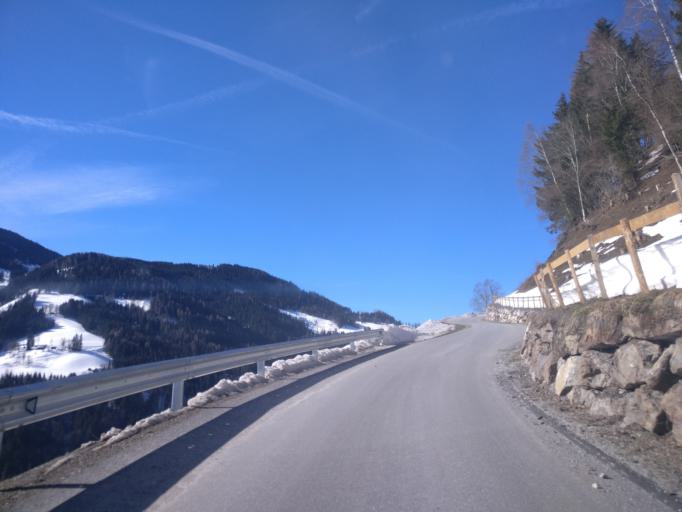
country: AT
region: Salzburg
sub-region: Politischer Bezirk Sankt Johann im Pongau
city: Sankt Johann im Pongau
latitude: 47.3342
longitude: 13.2366
